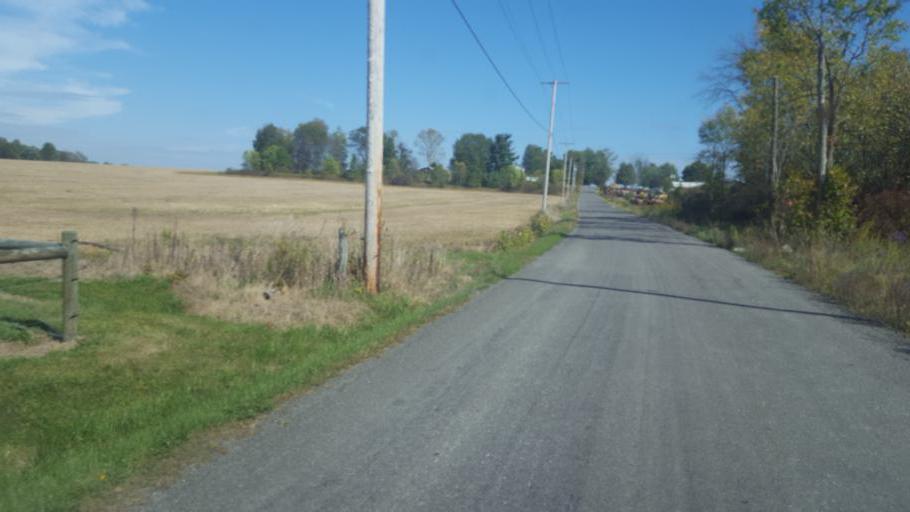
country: US
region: Pennsylvania
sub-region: Mercer County
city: Reynolds Heights
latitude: 41.3293
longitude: -80.3032
